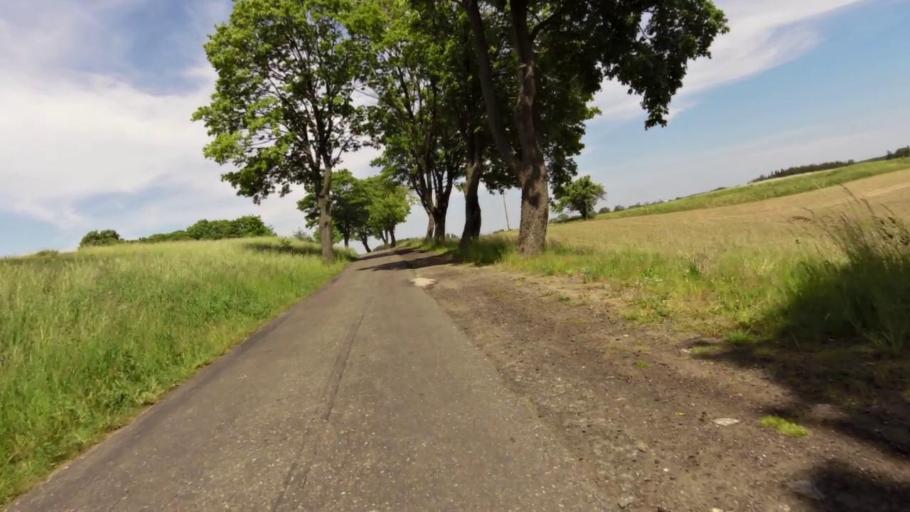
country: PL
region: West Pomeranian Voivodeship
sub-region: Powiat szczecinecki
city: Szczecinek
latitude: 53.6546
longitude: 16.6724
